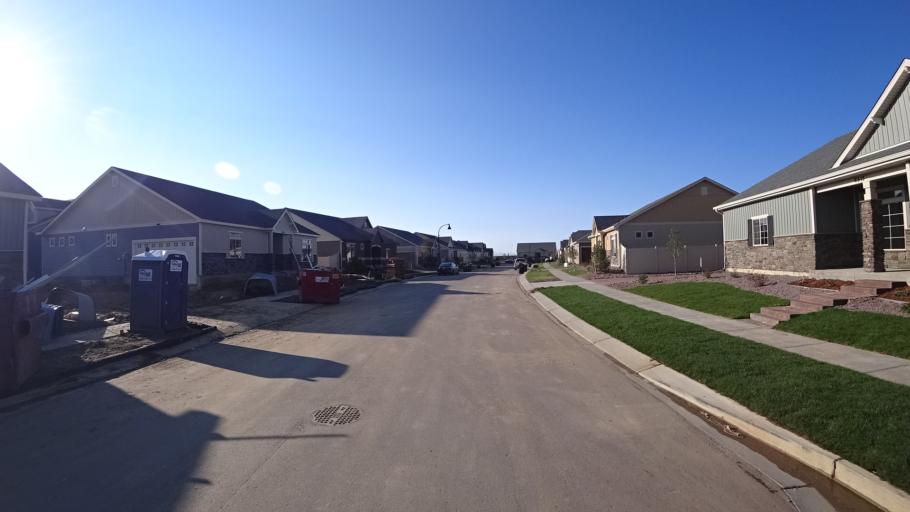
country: US
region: Colorado
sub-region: El Paso County
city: Cimarron Hills
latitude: 38.9283
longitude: -104.6576
